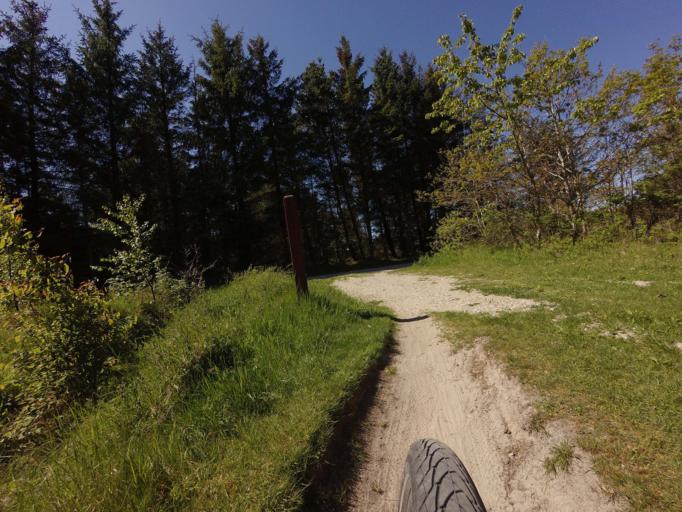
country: DK
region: North Denmark
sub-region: Jammerbugt Kommune
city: Pandrup
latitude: 57.2693
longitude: 9.6262
